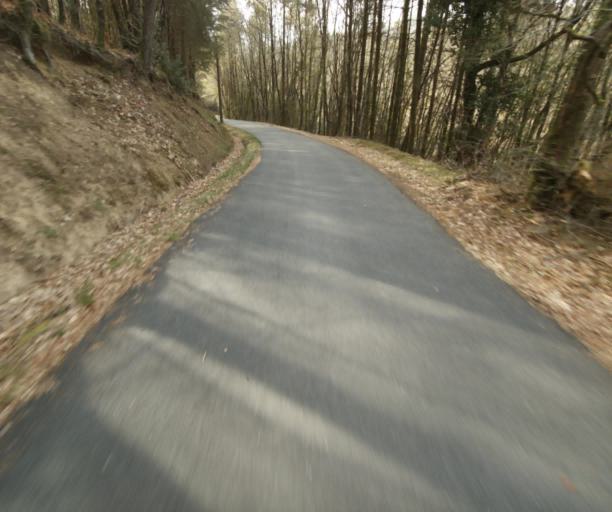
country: FR
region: Limousin
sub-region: Departement de la Correze
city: Chamboulive
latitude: 45.4293
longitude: 1.7912
